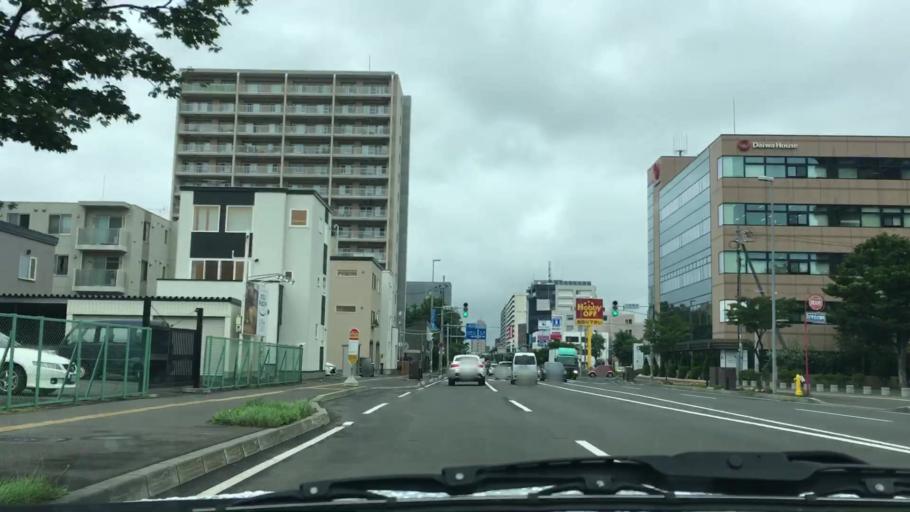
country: JP
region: Hokkaido
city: Sapporo
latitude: 43.0702
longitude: 141.3657
